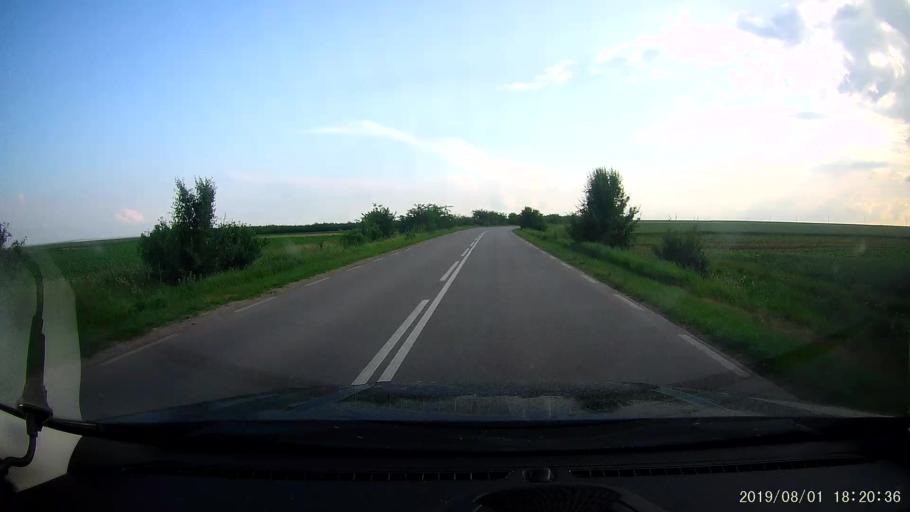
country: BG
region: Shumen
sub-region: Obshtina Kaolinovo
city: Kaolinovo
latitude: 43.6680
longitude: 27.0867
